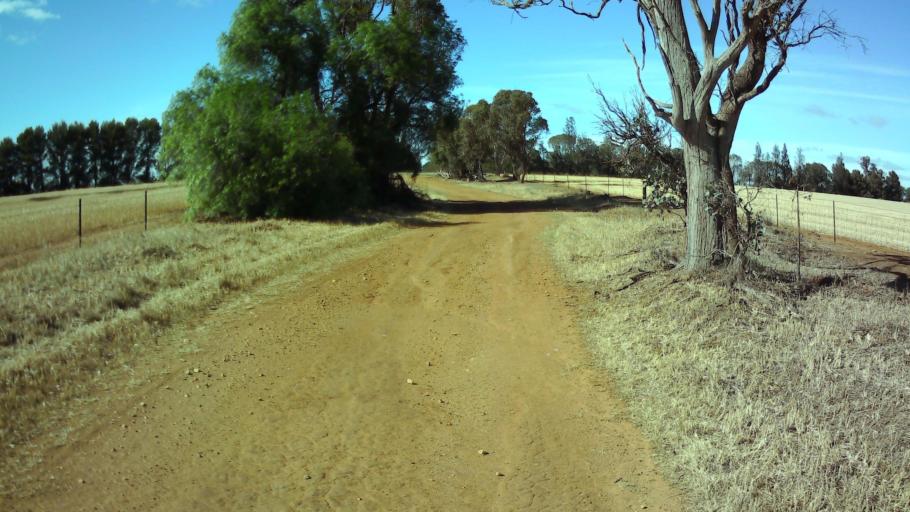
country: AU
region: New South Wales
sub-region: Weddin
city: Grenfell
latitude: -34.0602
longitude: 148.2673
